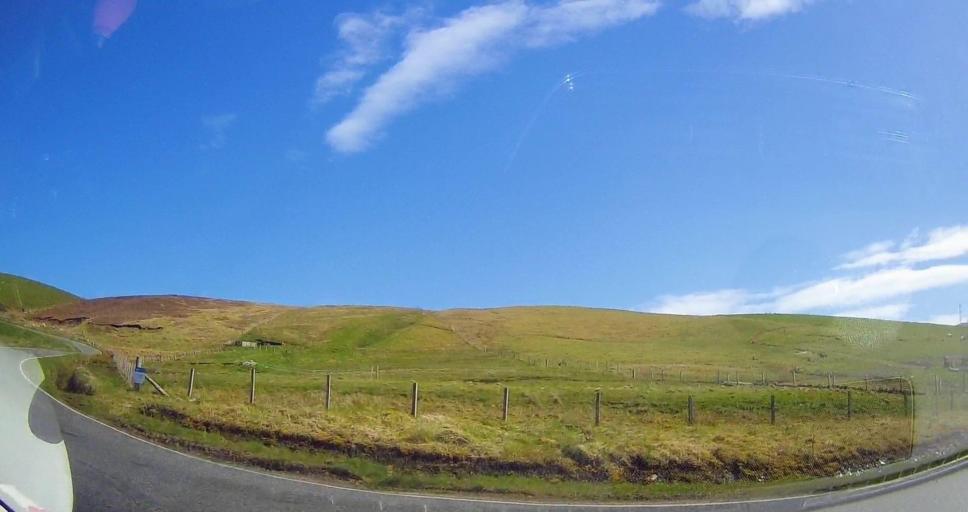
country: GB
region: Scotland
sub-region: Shetland Islands
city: Sandwick
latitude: 59.9724
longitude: -1.3159
